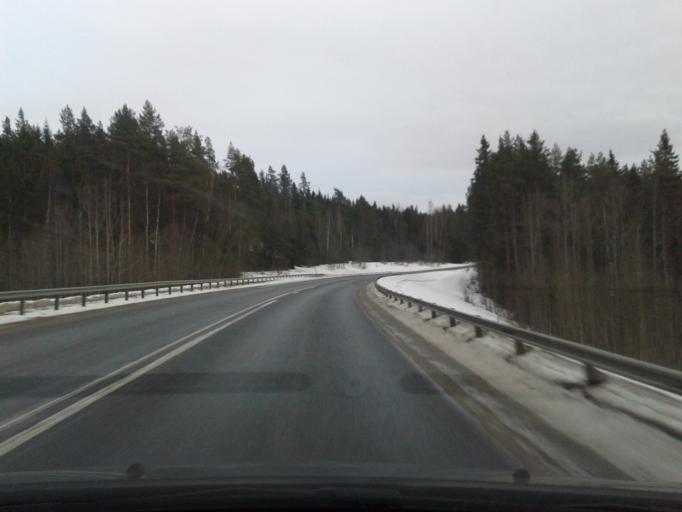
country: SE
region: Vaesternorrland
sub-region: Solleftea Kommun
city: As
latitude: 63.4136
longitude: 16.9652
